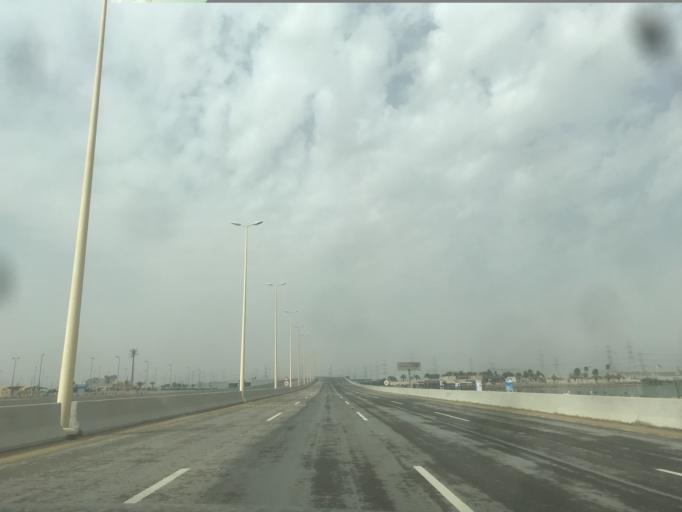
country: SA
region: Eastern Province
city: Dhahran
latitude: 26.2027
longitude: 50.0336
